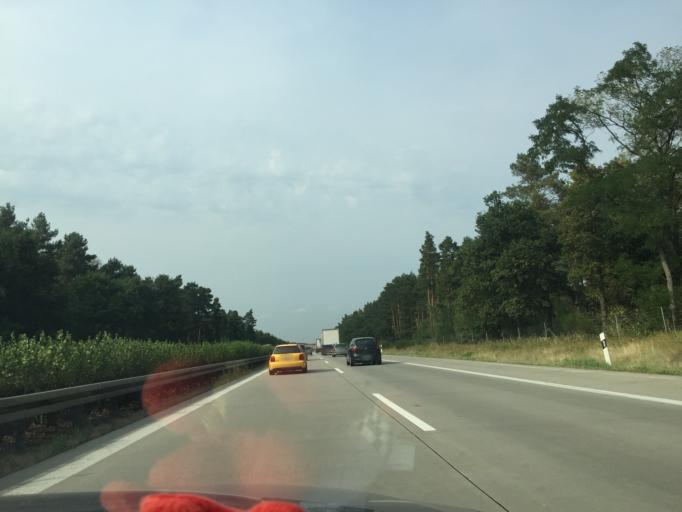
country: DE
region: Brandenburg
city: Teupitz
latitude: 52.0967
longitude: 13.6479
